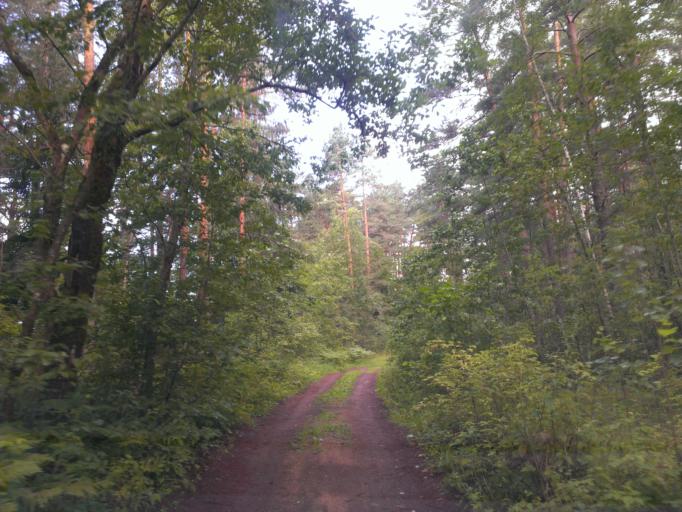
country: LV
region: Incukalns
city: Vangazi
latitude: 57.1023
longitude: 24.5309
